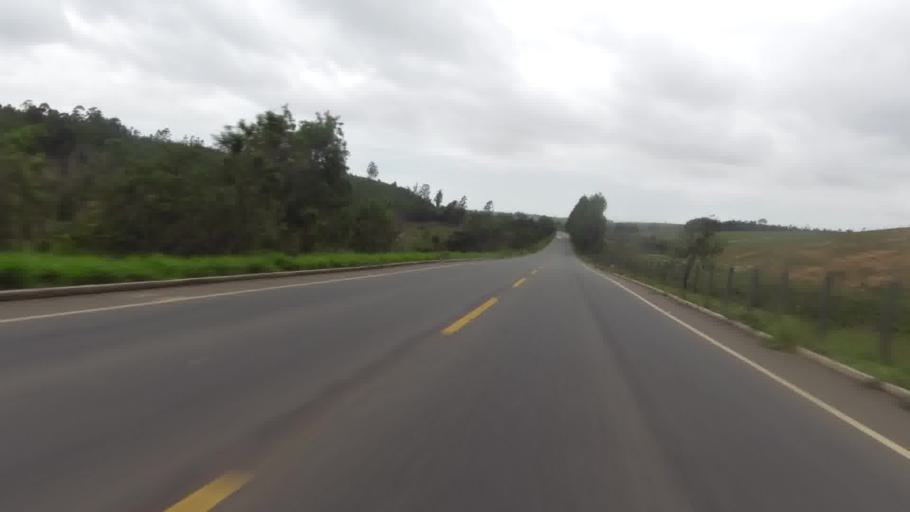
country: BR
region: Espirito Santo
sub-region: Piuma
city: Piuma
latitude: -20.7937
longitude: -40.7505
